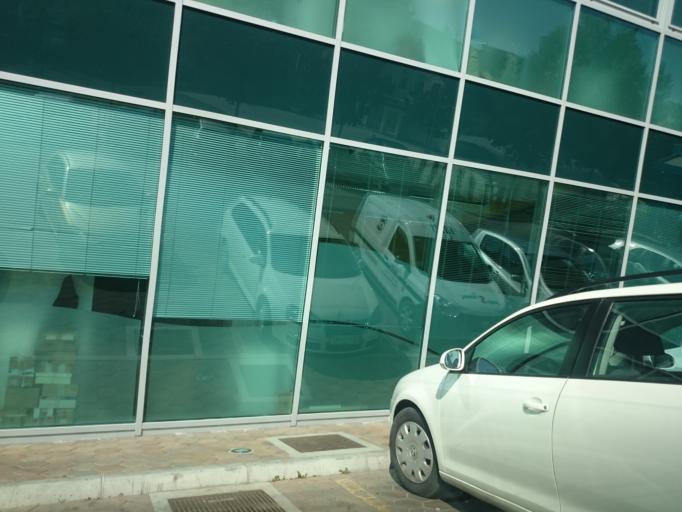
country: SI
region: Sentjur pri Celju
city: Sentjur
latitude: 46.2151
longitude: 15.3915
